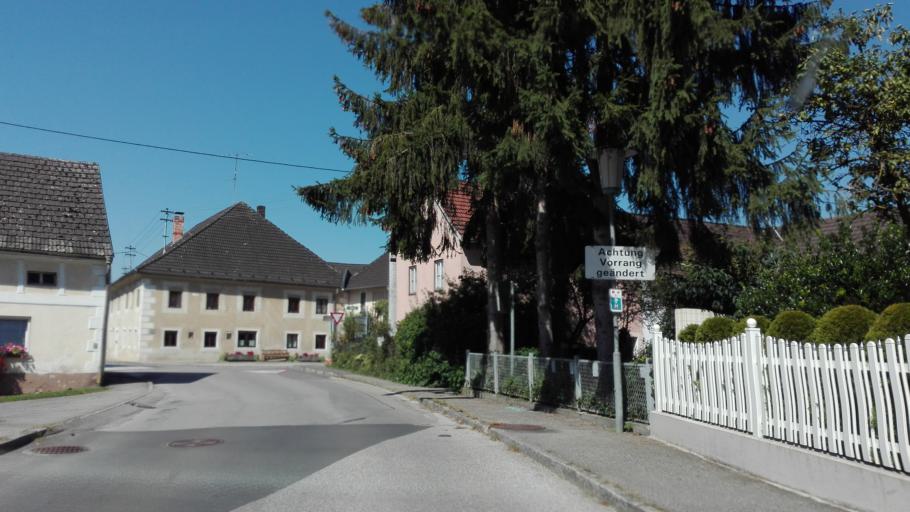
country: AT
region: Upper Austria
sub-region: Politischer Bezirk Perg
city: Perg
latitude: 48.2288
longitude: 14.7041
